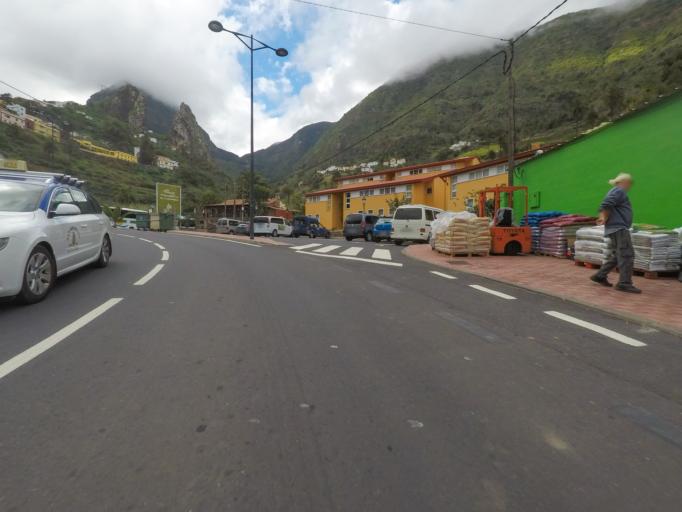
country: ES
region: Canary Islands
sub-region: Provincia de Santa Cruz de Tenerife
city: Hermigua
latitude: 28.1537
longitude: -17.1990
